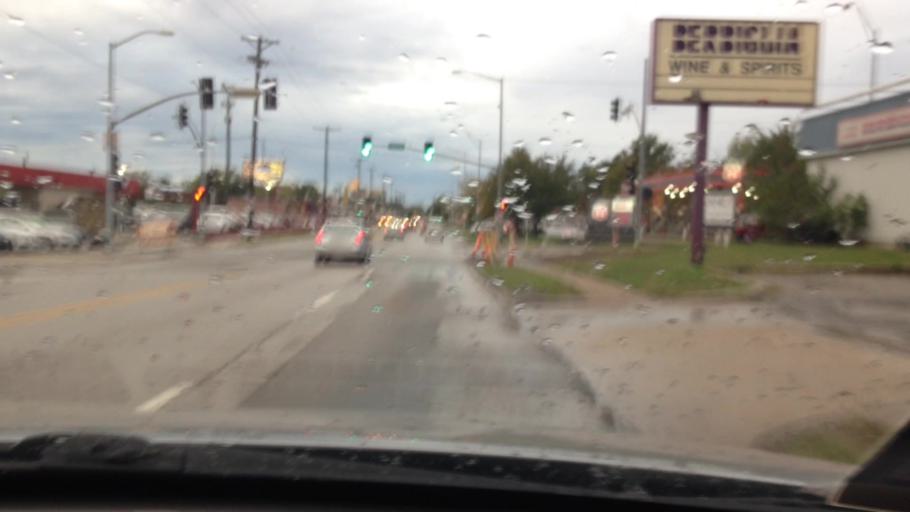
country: US
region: Kansas
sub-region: Johnson County
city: Leawood
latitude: 38.9855
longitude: -94.5946
